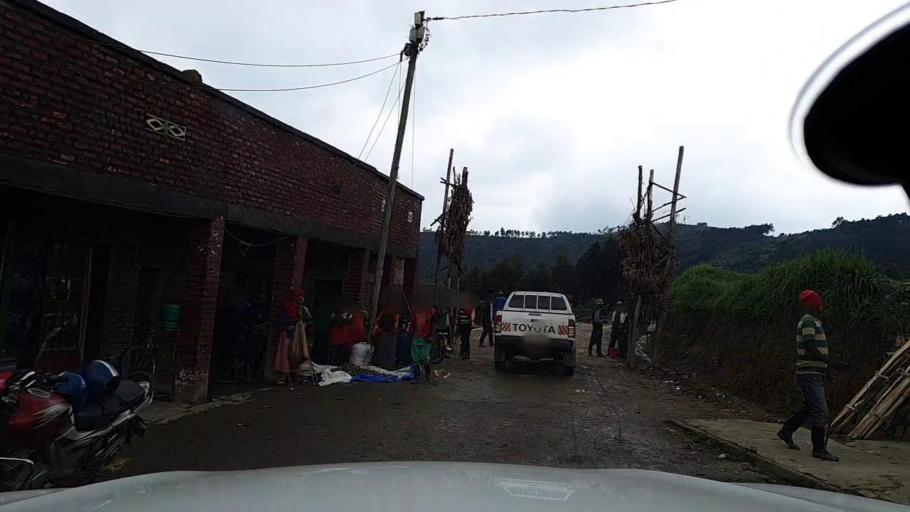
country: RW
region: Western Province
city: Kibuye
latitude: -2.0584
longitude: 29.5099
